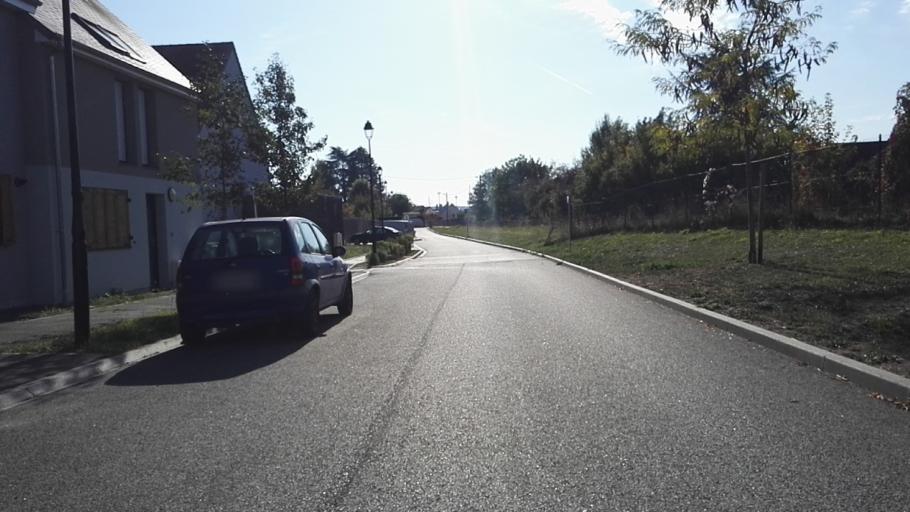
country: FR
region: Haute-Normandie
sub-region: Departement de l'Eure
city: Menilles
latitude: 49.0317
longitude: 1.3667
